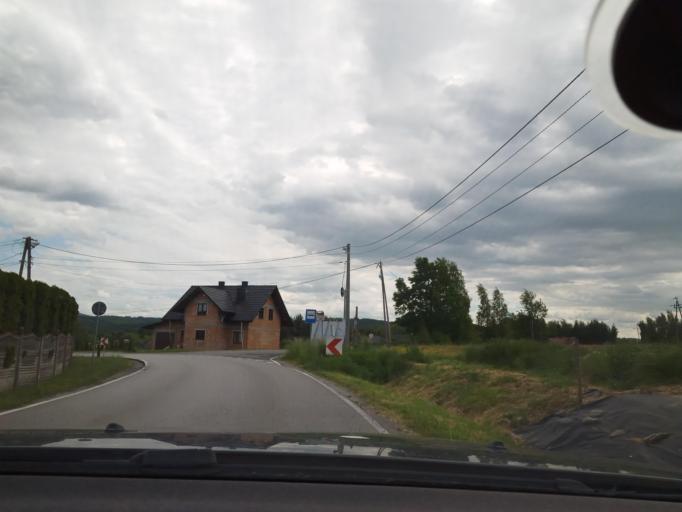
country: PL
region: Lesser Poland Voivodeship
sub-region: Powiat bochenski
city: Lapanow
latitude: 49.8373
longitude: 20.2746
